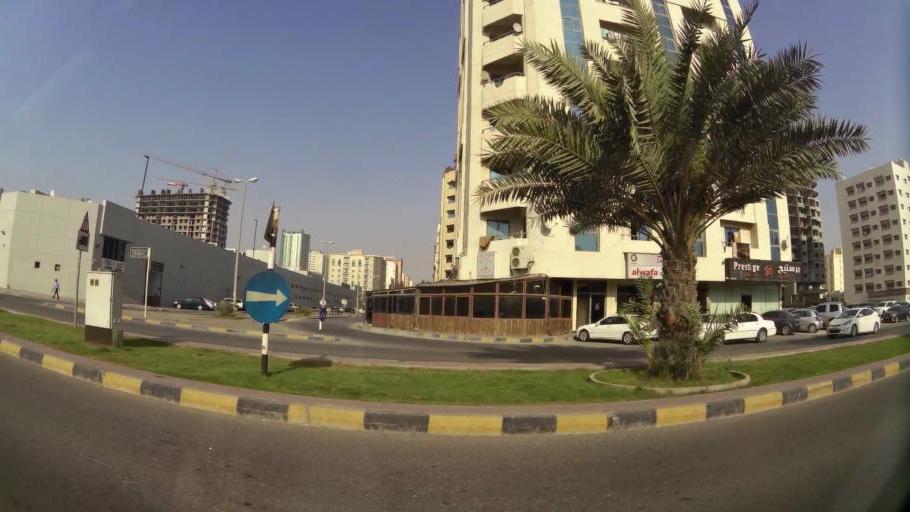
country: AE
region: Ajman
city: Ajman
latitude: 25.3890
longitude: 55.4458
